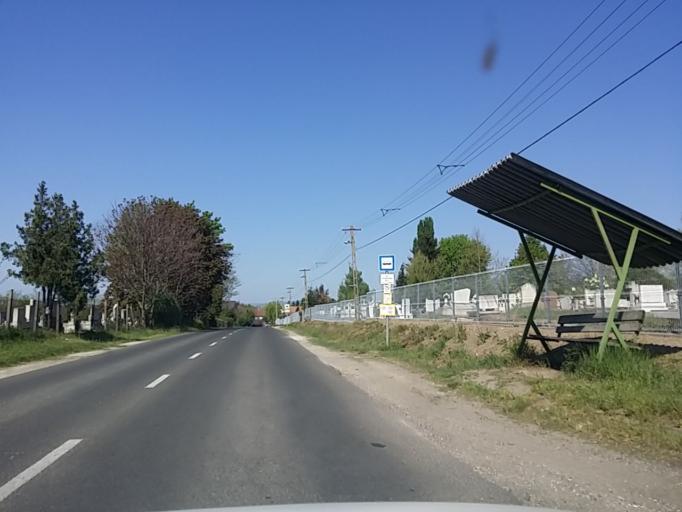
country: HU
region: Pest
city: Fot
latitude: 47.6034
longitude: 19.2080
